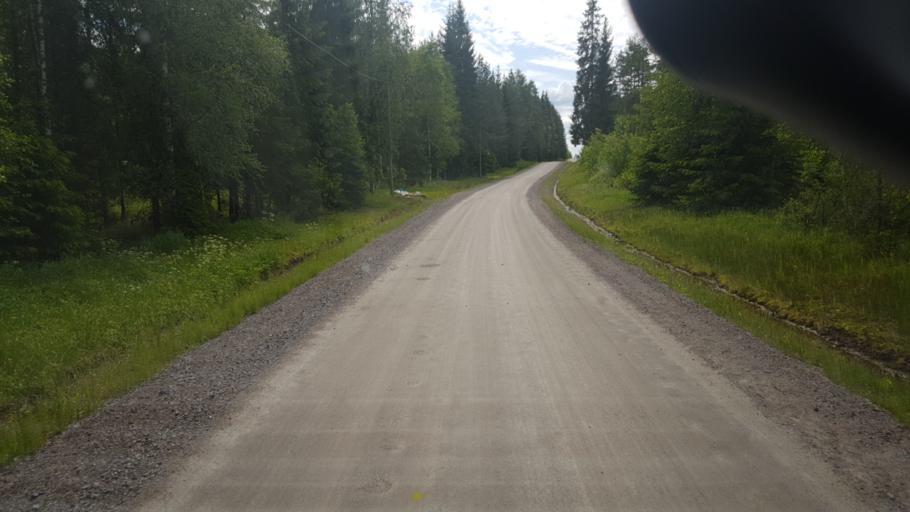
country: SE
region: Vaermland
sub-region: Eda Kommun
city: Charlottenberg
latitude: 59.8979
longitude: 12.3805
